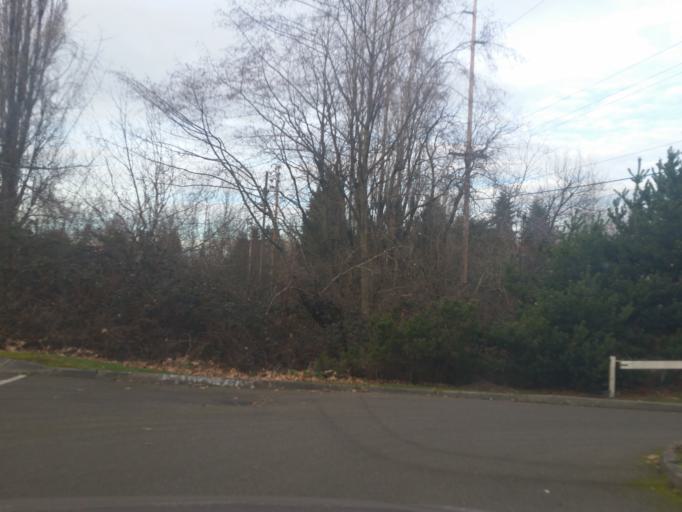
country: US
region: Washington
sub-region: King County
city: Shoreline
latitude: 47.7382
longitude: -122.3294
